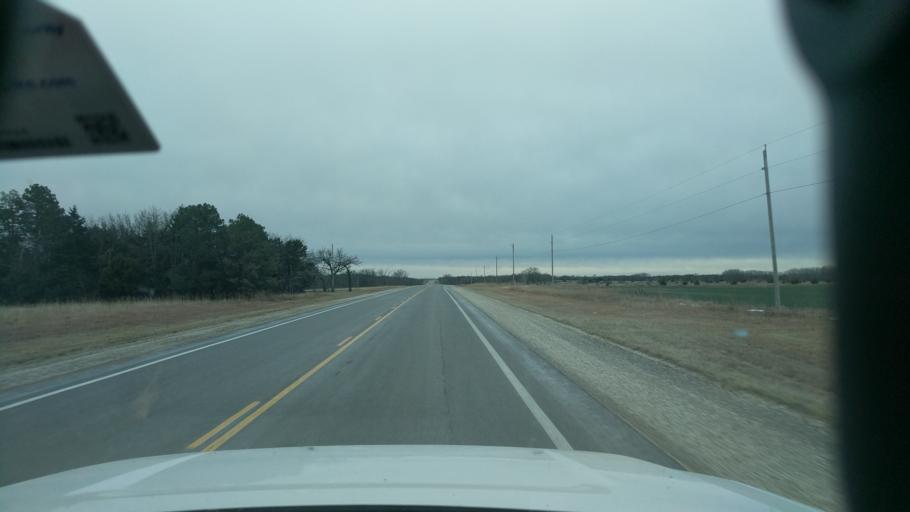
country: US
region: Kansas
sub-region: Marion County
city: Marion
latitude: 38.4806
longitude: -96.9577
